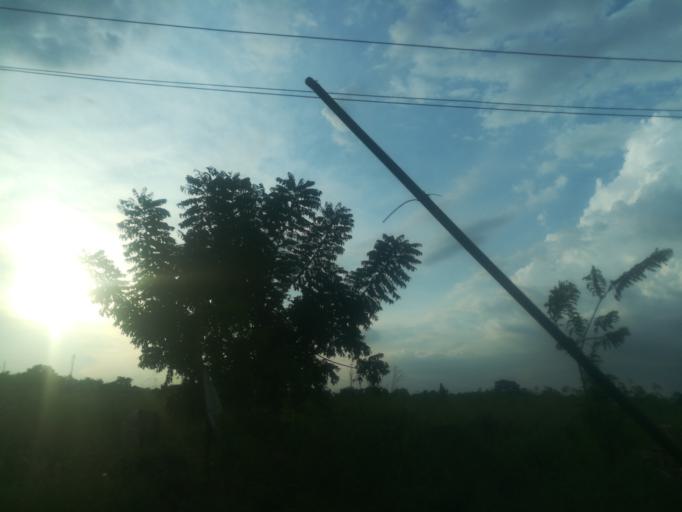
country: NG
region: Oyo
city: Ibadan
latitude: 7.3818
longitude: 3.8465
